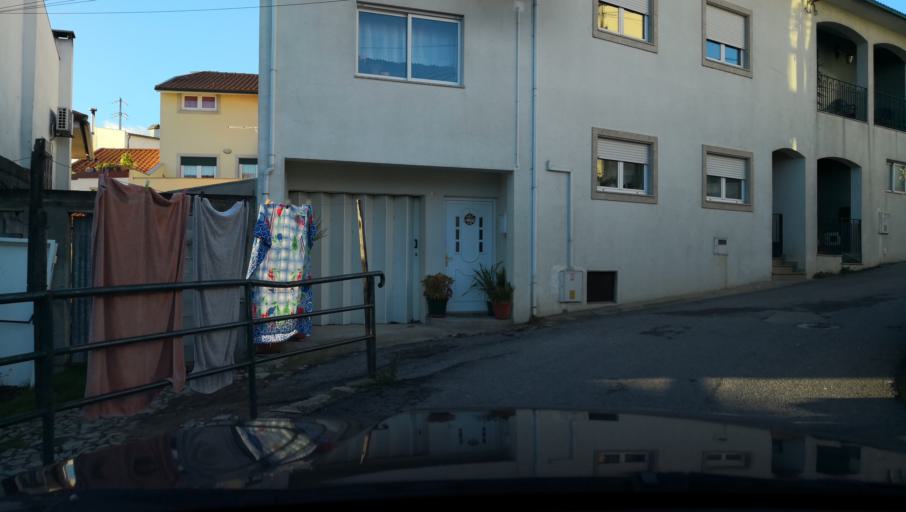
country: PT
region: Vila Real
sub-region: Vila Real
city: Vila Real
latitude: 41.2799
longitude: -7.7412
